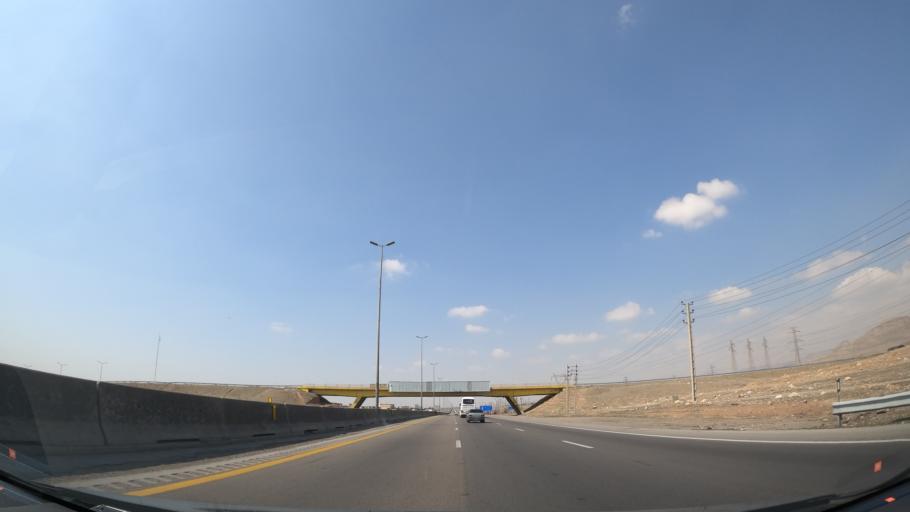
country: IR
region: Qazvin
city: Abyek
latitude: 36.0641
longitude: 50.4911
